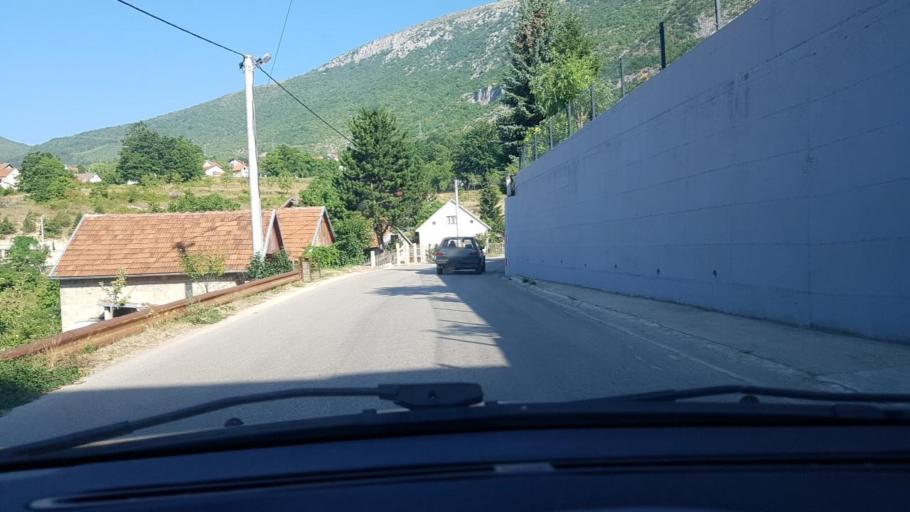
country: BA
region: Federation of Bosnia and Herzegovina
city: Rumboci
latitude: 43.8304
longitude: 17.5101
